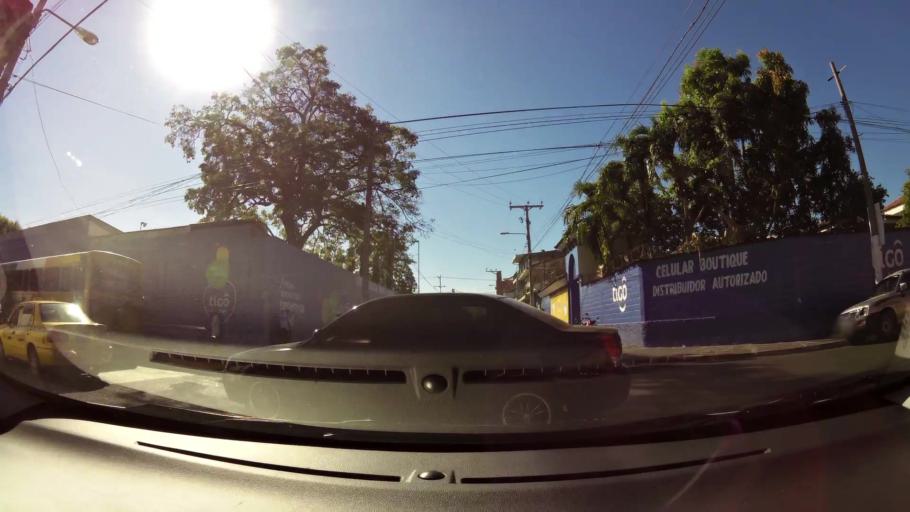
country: SV
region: San Miguel
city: San Miguel
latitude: 13.4857
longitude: -88.1774
